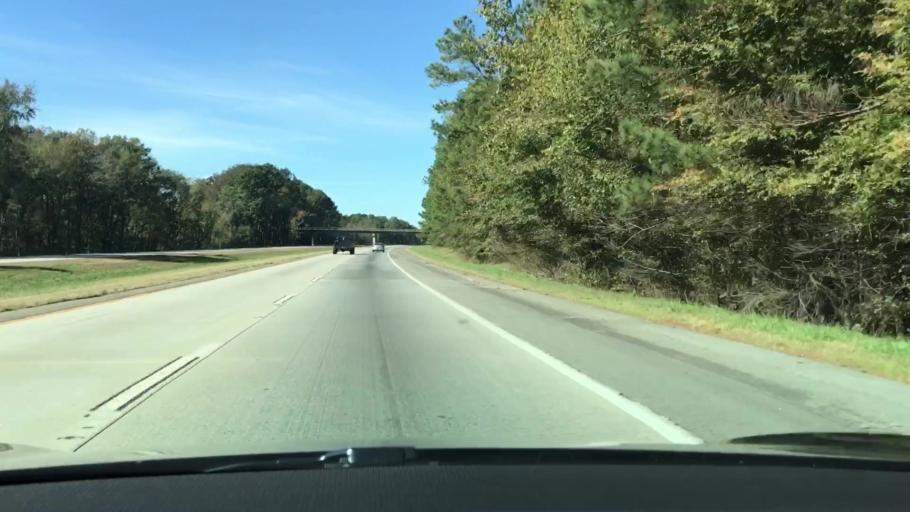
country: US
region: Georgia
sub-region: Taliaferro County
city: Crawfordville
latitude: 33.5280
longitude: -82.9530
